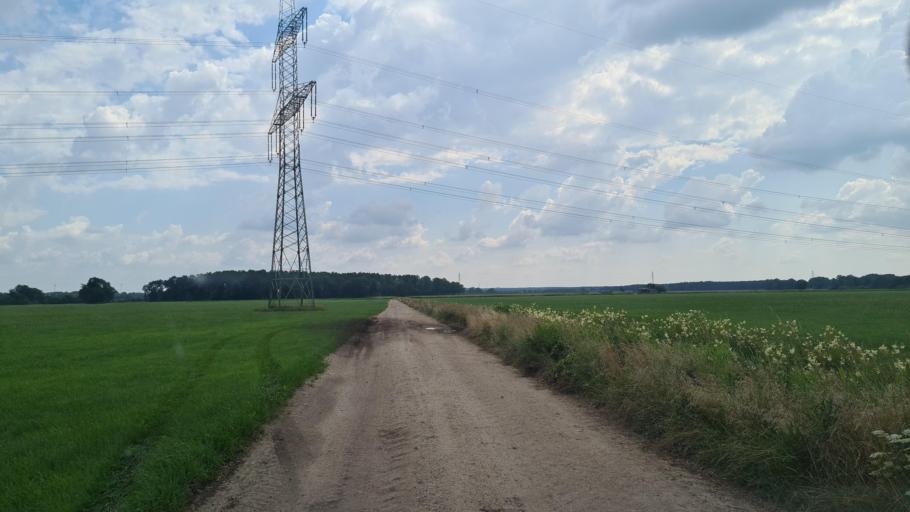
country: DE
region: Brandenburg
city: Sallgast
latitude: 51.6301
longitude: 13.8662
